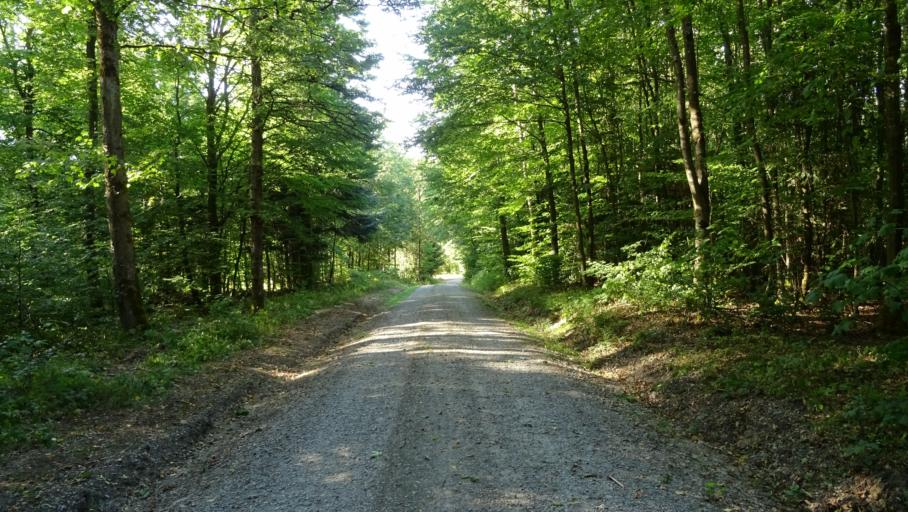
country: DE
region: Baden-Wuerttemberg
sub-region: Karlsruhe Region
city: Fahrenbach
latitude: 49.4104
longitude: 9.1138
